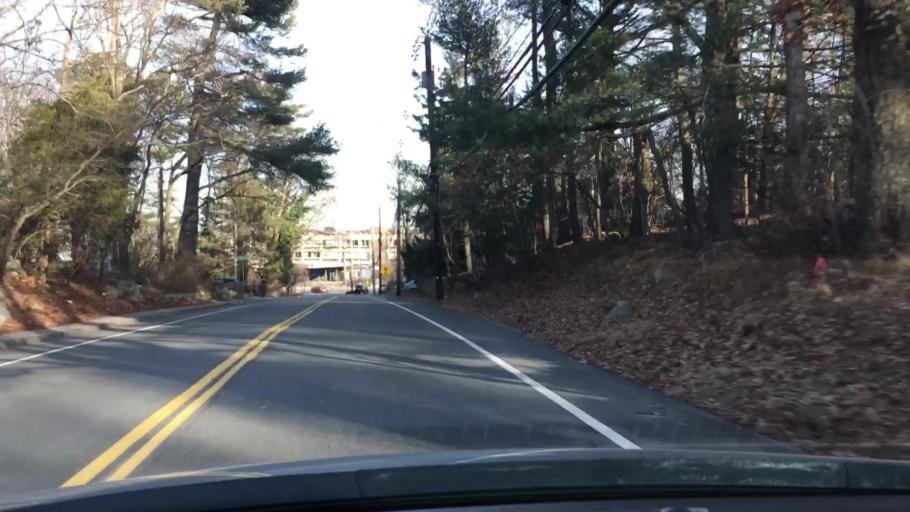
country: US
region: Massachusetts
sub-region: Norfolk County
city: Dedham
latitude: 42.2280
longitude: -71.1881
